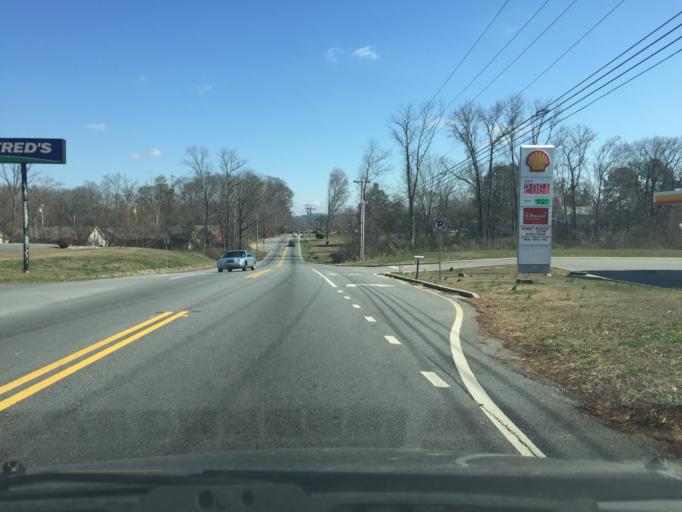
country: US
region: Georgia
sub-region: Catoosa County
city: Fort Oglethorpe
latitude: 34.9570
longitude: -85.2330
